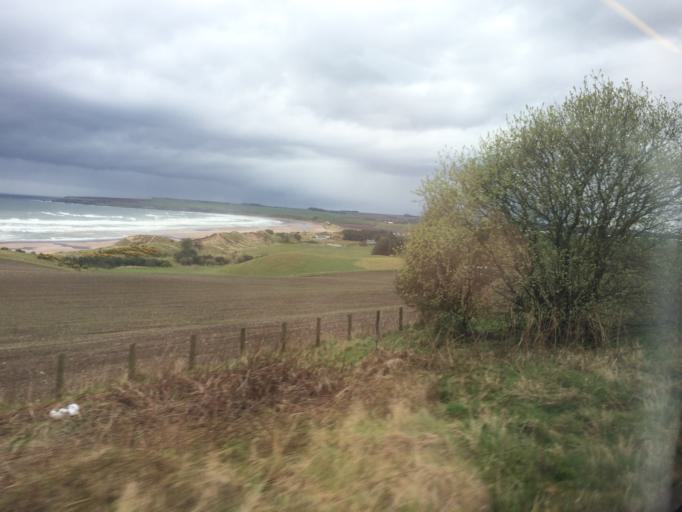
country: GB
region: Scotland
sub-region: Angus
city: Montrose
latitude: 56.6626
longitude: -2.5042
